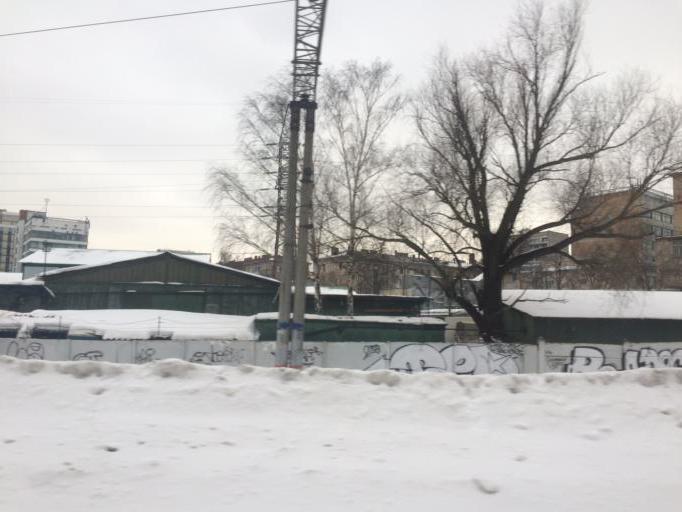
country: RU
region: Moscow
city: Sokol
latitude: 55.8049
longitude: 37.5569
